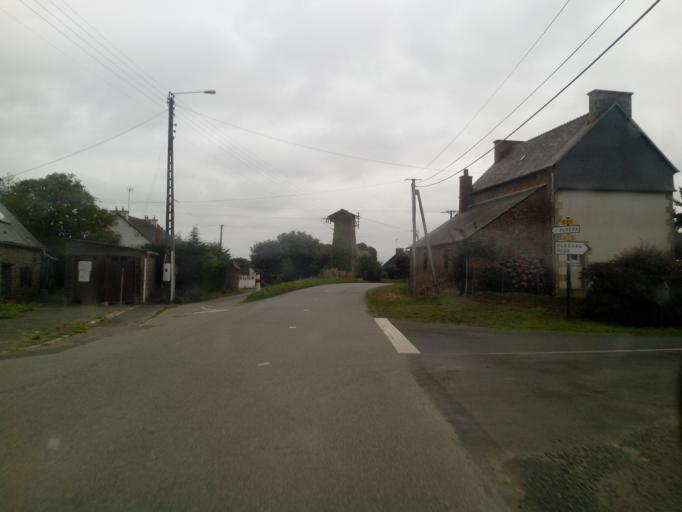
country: FR
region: Brittany
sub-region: Departement des Cotes-d'Armor
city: Plehedel
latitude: 48.6861
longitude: -3.0003
